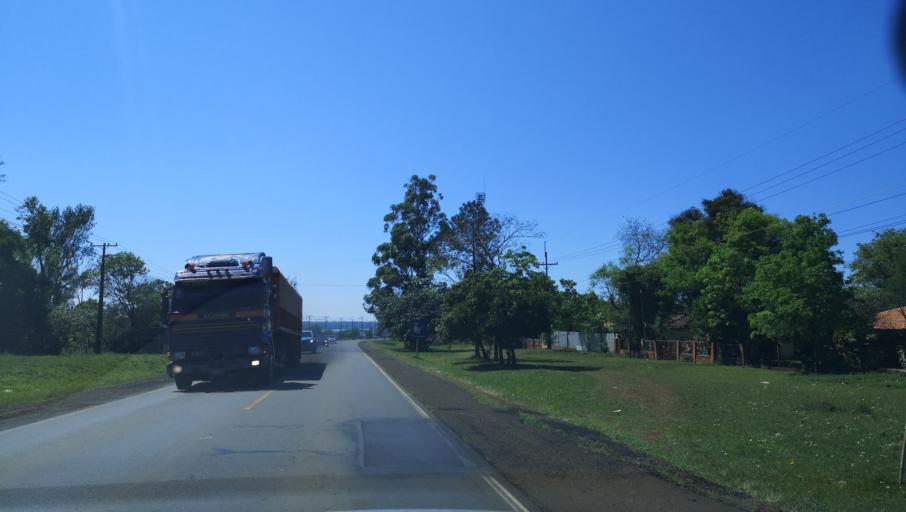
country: PY
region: Itapua
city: Carmen del Parana
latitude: -27.1926
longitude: -56.1963
